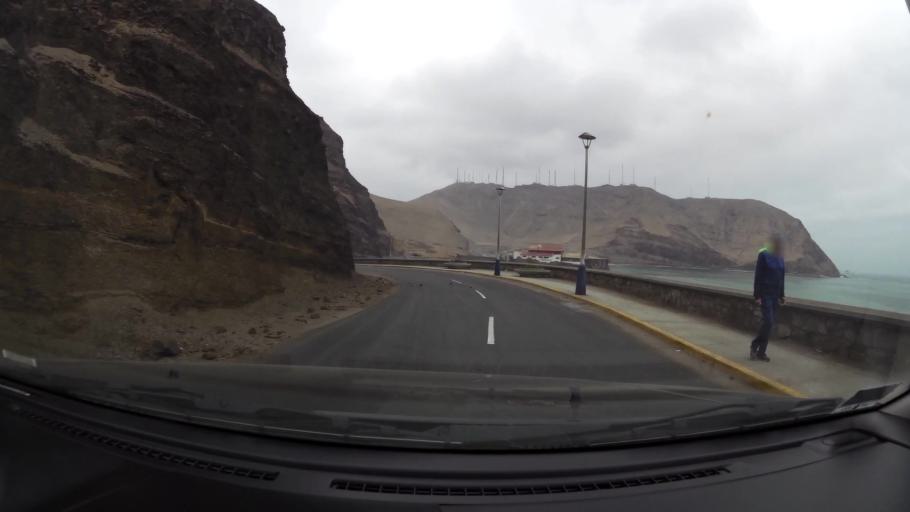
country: PE
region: Lima
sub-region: Lima
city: Surco
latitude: -12.1690
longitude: -77.0370
